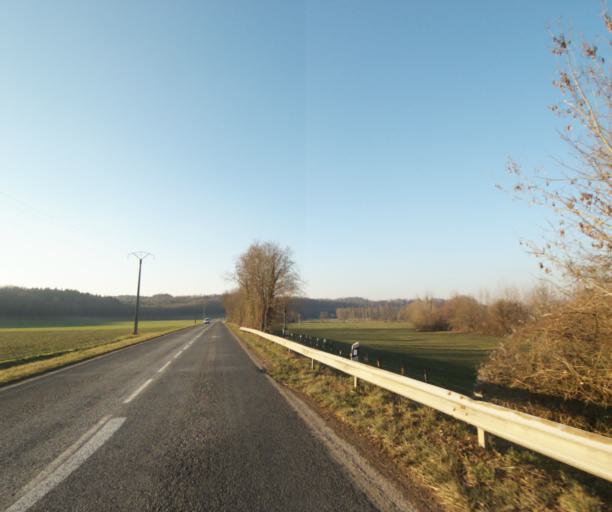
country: FR
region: Champagne-Ardenne
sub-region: Departement de la Haute-Marne
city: Bienville
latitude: 48.5649
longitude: 5.0468
